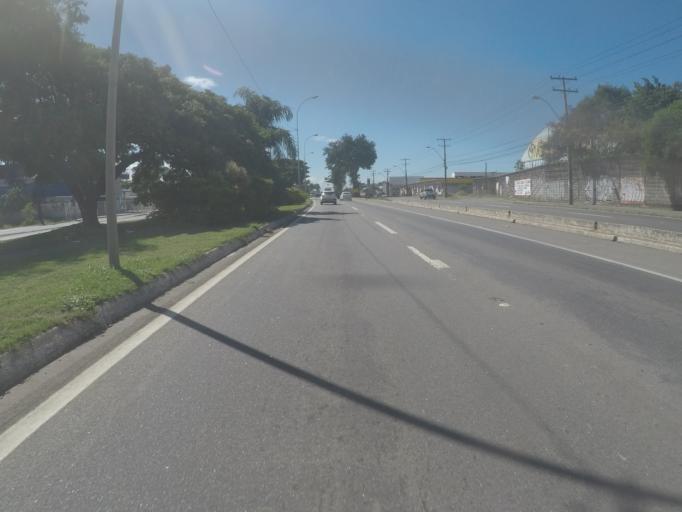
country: BR
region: Espirito Santo
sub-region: Serra
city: Serra
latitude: -20.2094
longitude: -40.2694
